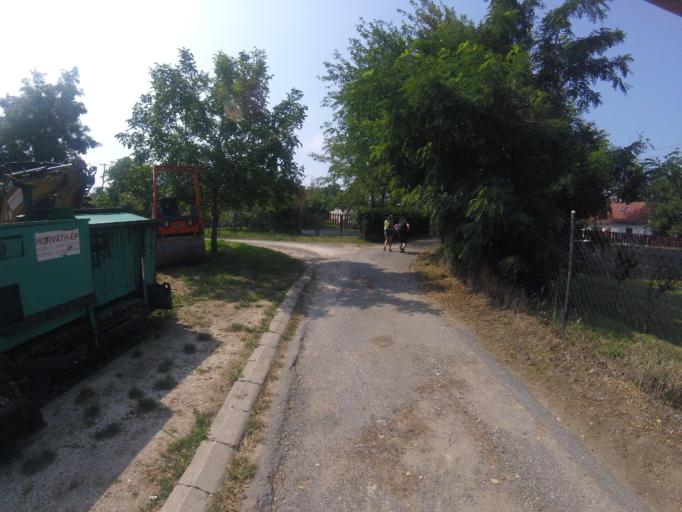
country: HU
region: Veszprem
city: Badacsonytomaj
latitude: 46.8159
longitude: 17.4906
